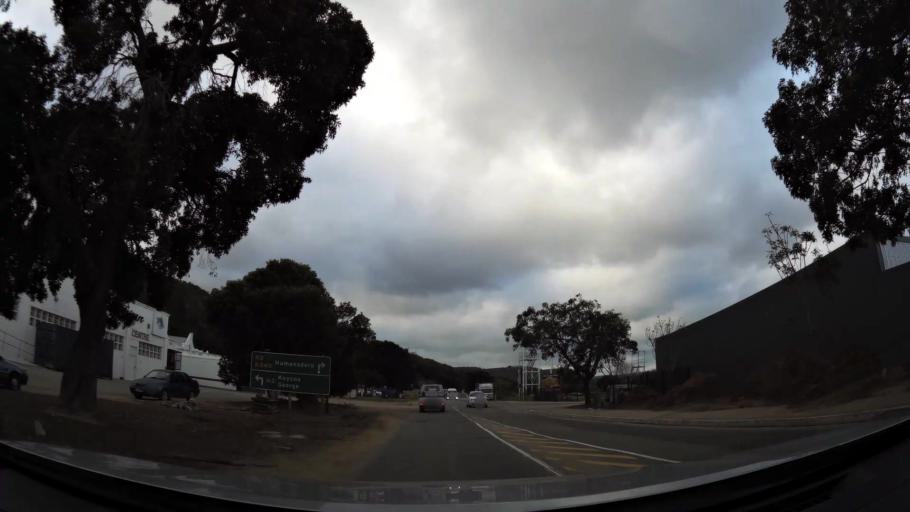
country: ZA
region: Western Cape
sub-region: Eden District Municipality
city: Plettenberg Bay
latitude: -34.0418
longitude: 23.3705
